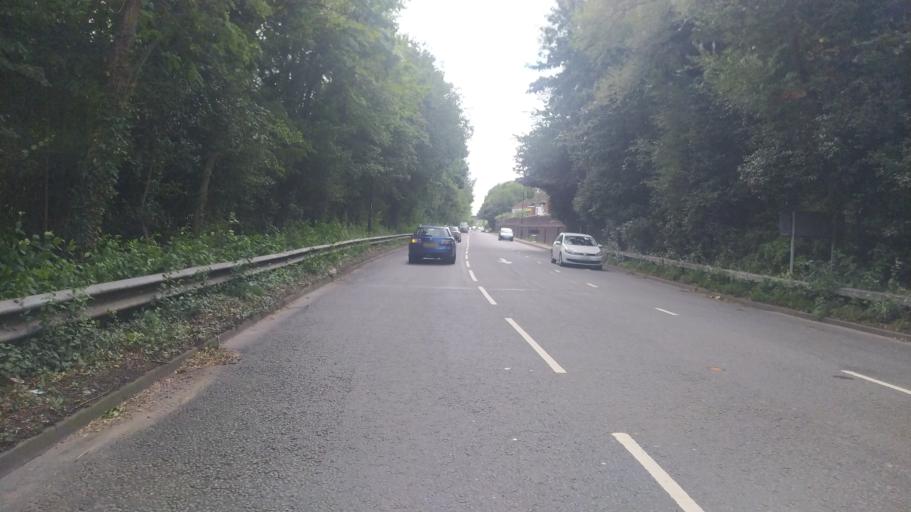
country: GB
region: England
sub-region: Hampshire
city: Eastleigh
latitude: 50.9400
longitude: -1.3777
